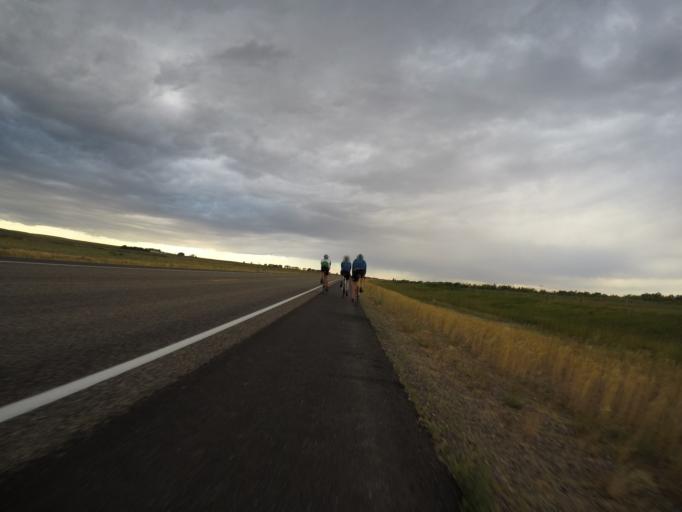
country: US
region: Wyoming
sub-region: Albany County
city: Laramie
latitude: 41.7741
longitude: -105.9803
